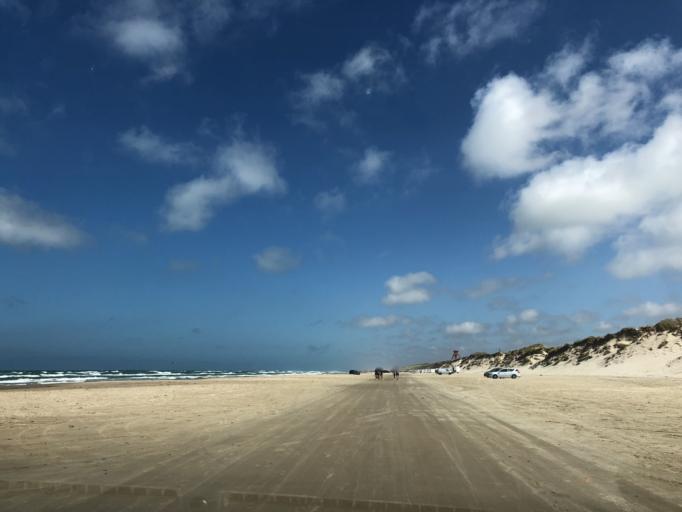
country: DK
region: North Denmark
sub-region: Jammerbugt Kommune
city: Pandrup
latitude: 57.2497
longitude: 9.5725
